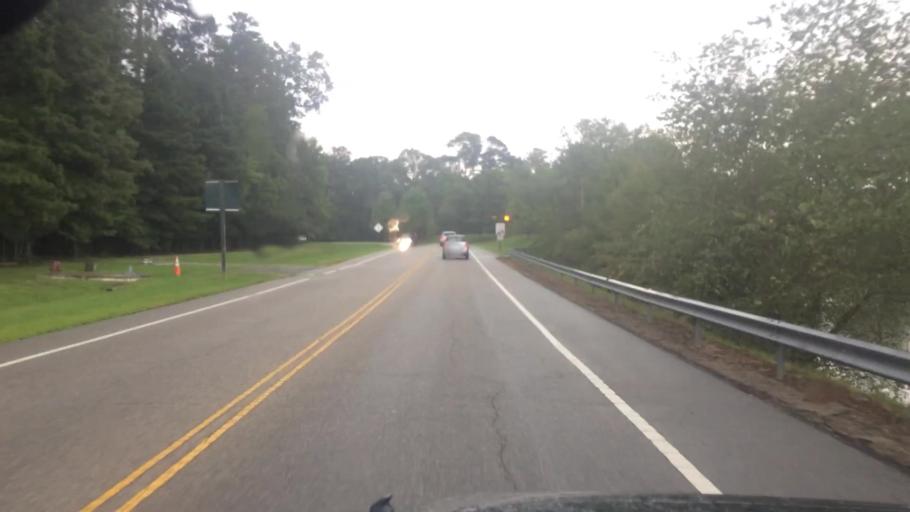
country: US
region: Virginia
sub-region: James City County
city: Williamsburg
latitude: 37.2601
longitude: -76.7373
